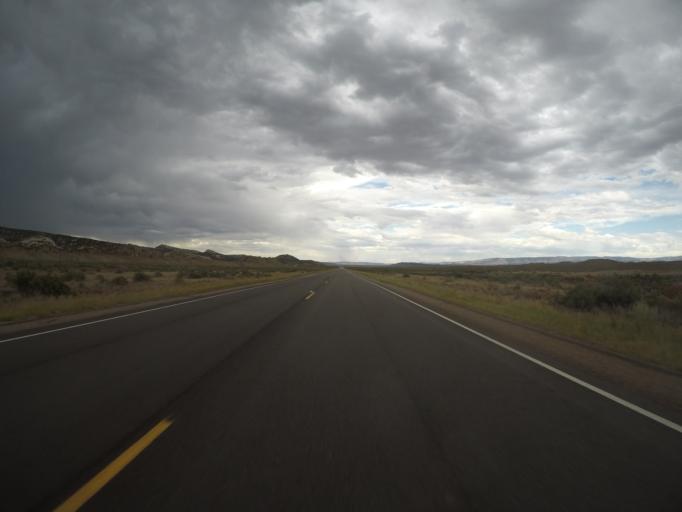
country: US
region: Colorado
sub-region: Rio Blanco County
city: Rangely
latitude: 40.2502
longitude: -108.7712
